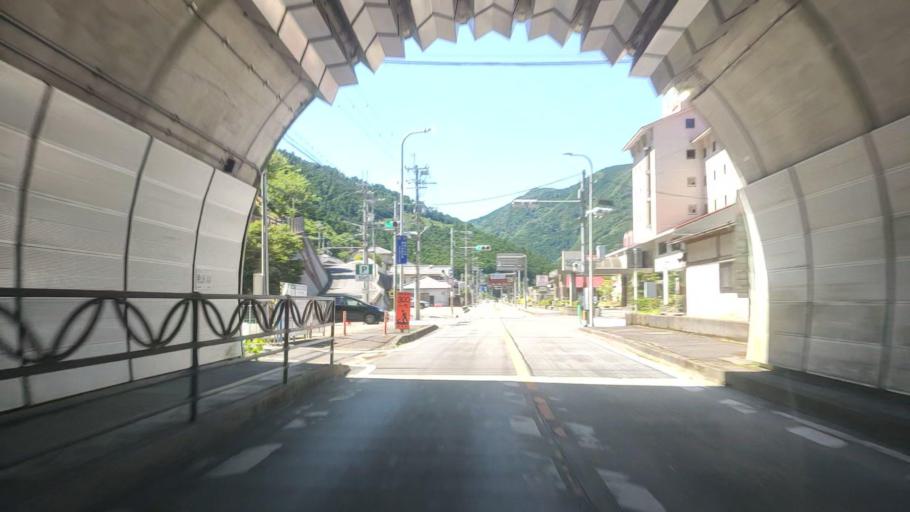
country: JP
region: Nara
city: Yoshino-cho
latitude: 34.3370
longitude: 135.9545
